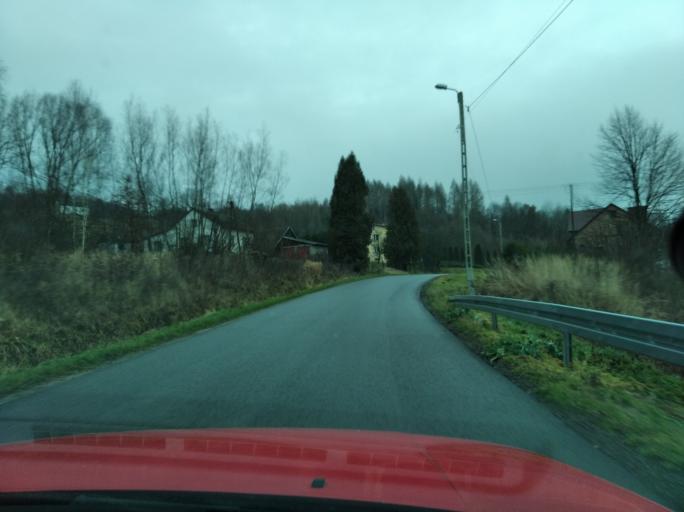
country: PL
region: Subcarpathian Voivodeship
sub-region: Powiat przemyski
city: Nienadowa
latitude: 49.8528
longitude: 22.4231
